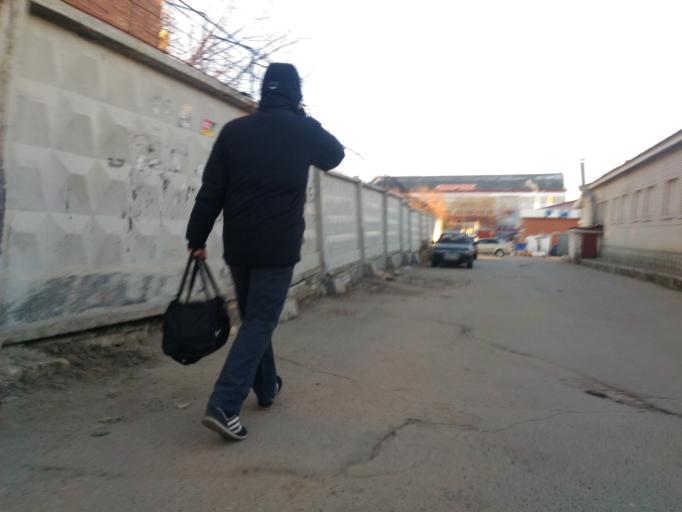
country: RU
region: Ulyanovsk
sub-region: Ulyanovskiy Rayon
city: Ulyanovsk
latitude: 54.3179
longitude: 48.3900
